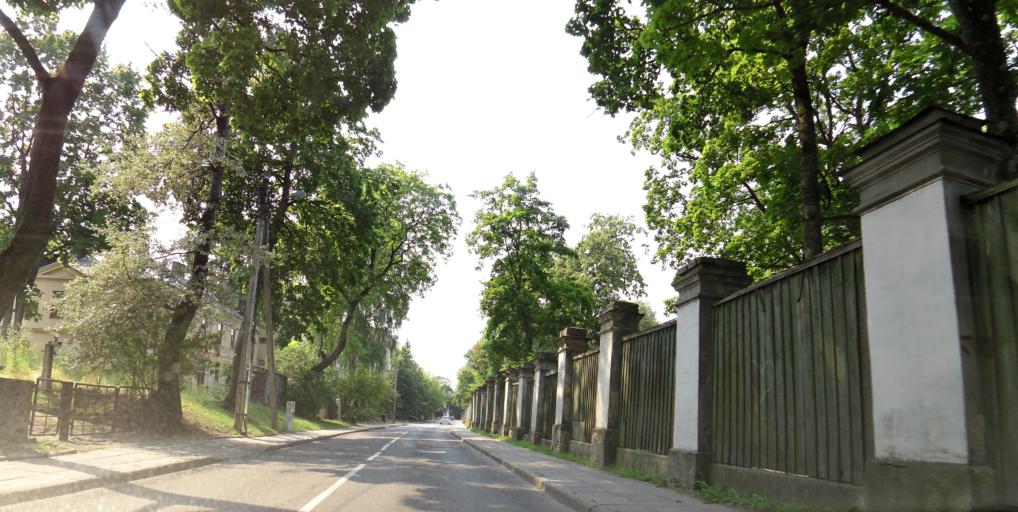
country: LT
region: Vilnius County
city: Rasos
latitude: 54.6980
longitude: 25.3128
